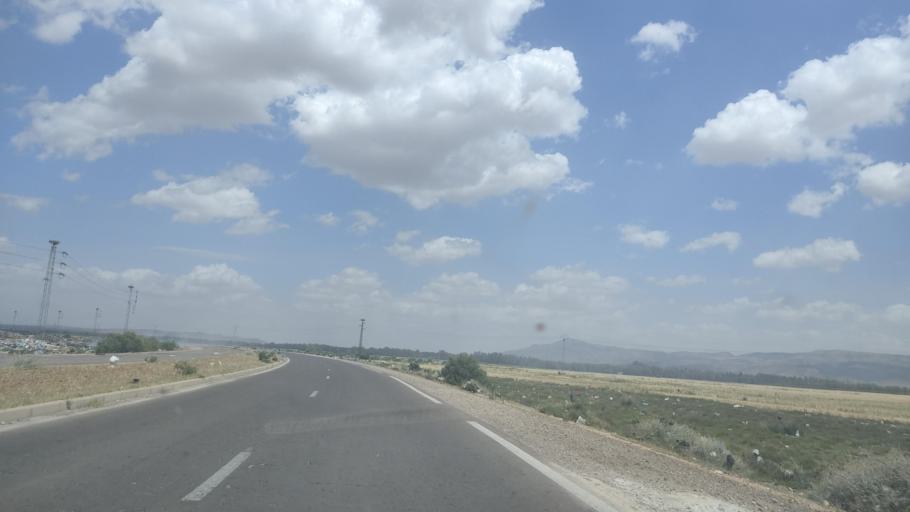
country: TN
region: Al Qasrayn
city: Kasserine
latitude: 35.1978
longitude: 8.8490
